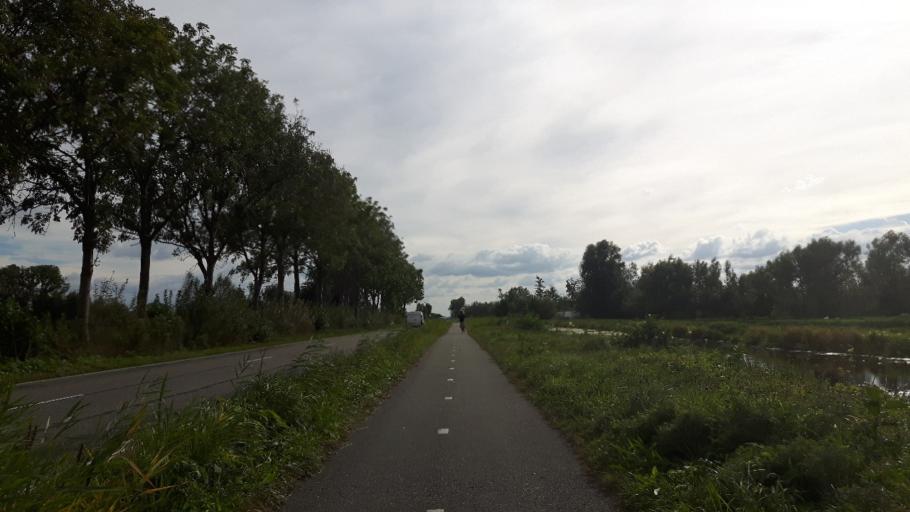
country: NL
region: Utrecht
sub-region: Gemeente De Ronde Venen
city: Mijdrecht
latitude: 52.1522
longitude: 4.8580
